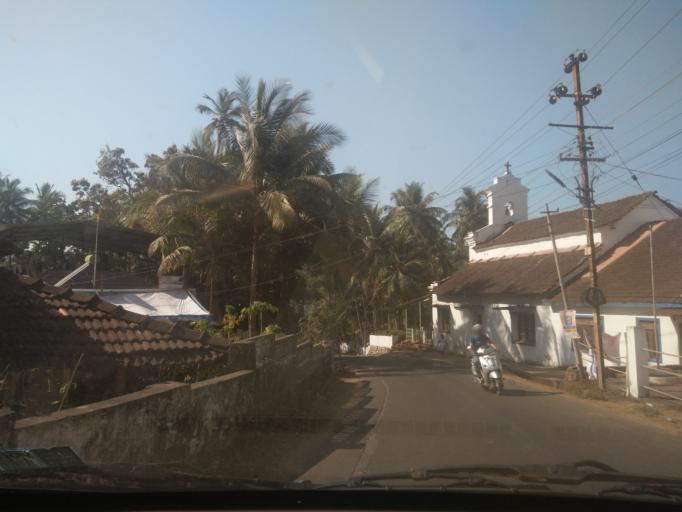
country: IN
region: Goa
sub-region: South Goa
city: Chicalim
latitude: 15.3706
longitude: 73.8388
